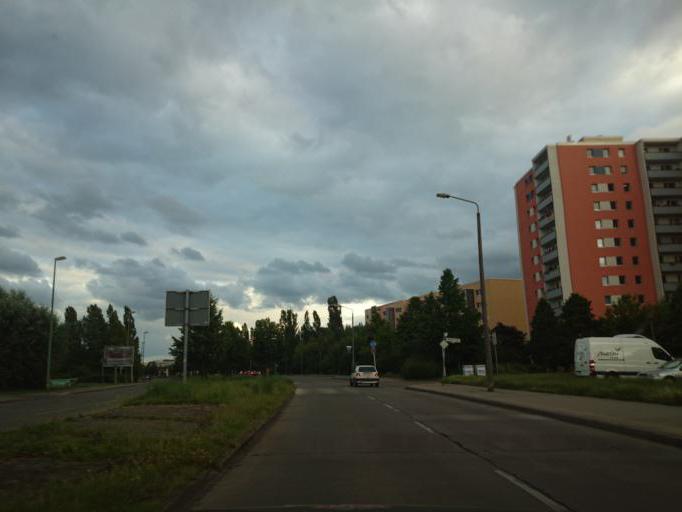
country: DE
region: Berlin
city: Hellersdorf
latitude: 52.5460
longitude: 13.6032
